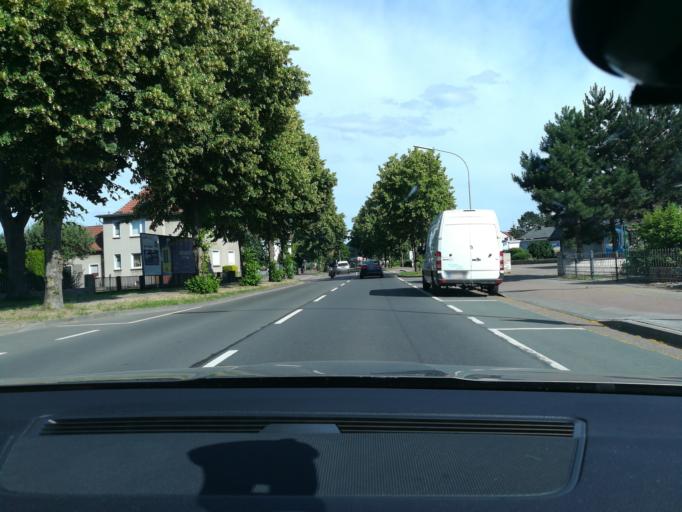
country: DE
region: North Rhine-Westphalia
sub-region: Regierungsbezirk Detmold
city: Minden
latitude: 52.3107
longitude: 8.8905
